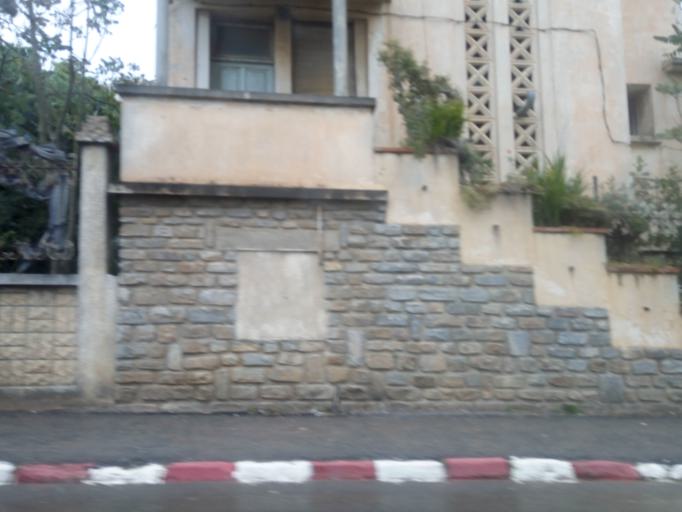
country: DZ
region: Tipaza
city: Saoula
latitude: 36.7323
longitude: 2.9930
